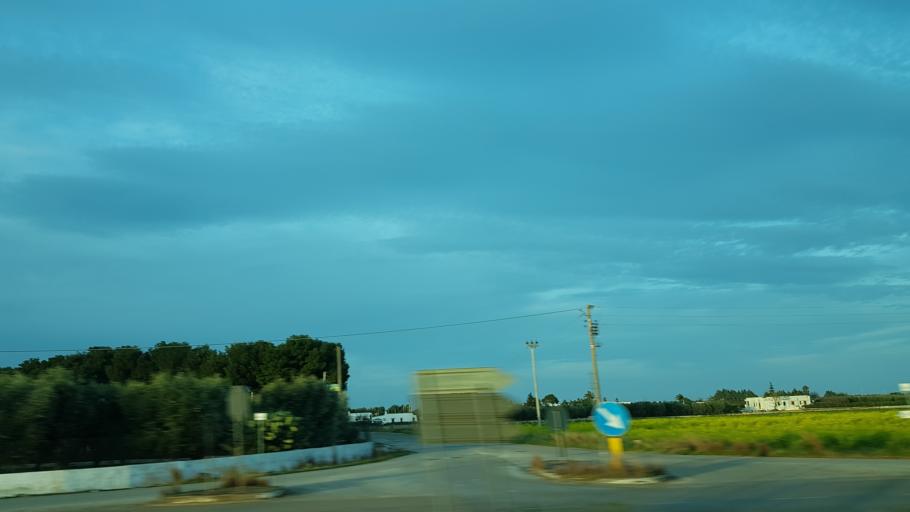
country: IT
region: Apulia
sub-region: Provincia di Brindisi
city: Carovigno
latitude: 40.7430
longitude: 17.7138
